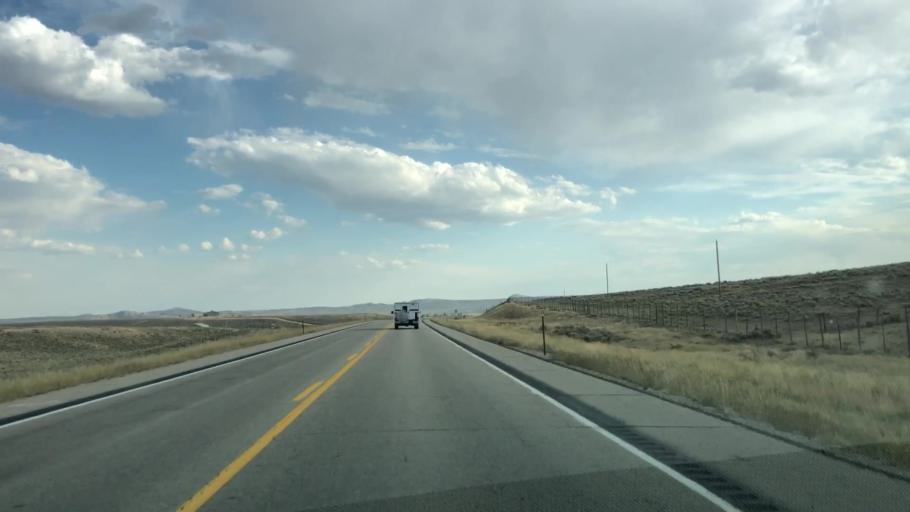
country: US
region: Wyoming
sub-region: Sublette County
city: Pinedale
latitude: 42.9040
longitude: -110.0759
